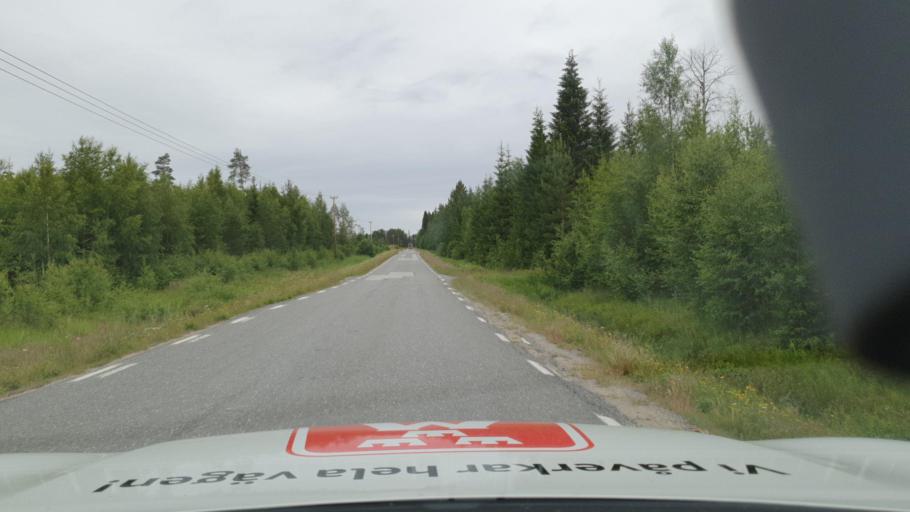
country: SE
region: Vaesterbotten
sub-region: Nordmalings Kommun
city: Nordmaling
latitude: 63.5166
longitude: 19.4214
